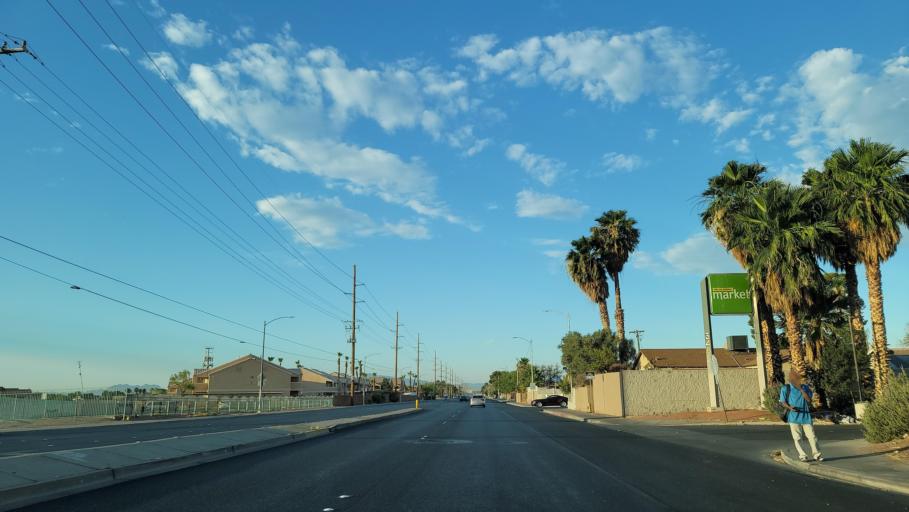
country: US
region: Nevada
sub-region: Clark County
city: North Las Vegas
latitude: 36.1953
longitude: -115.0985
